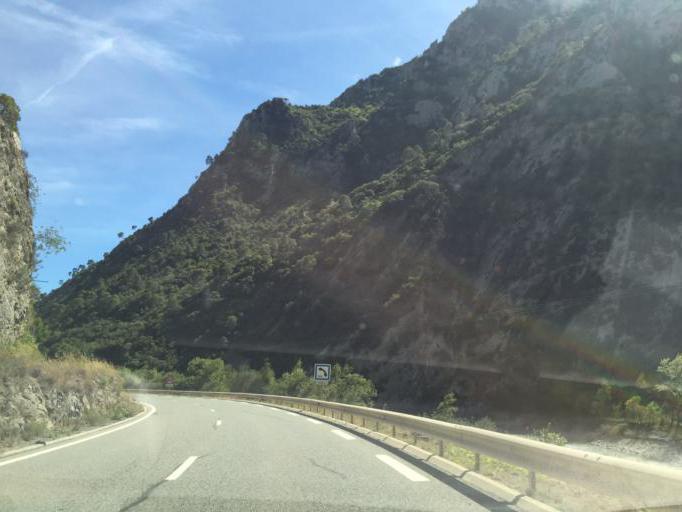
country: FR
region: Provence-Alpes-Cote d'Azur
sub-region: Departement des Alpes-Maritimes
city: Levens
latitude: 43.8751
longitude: 7.1927
